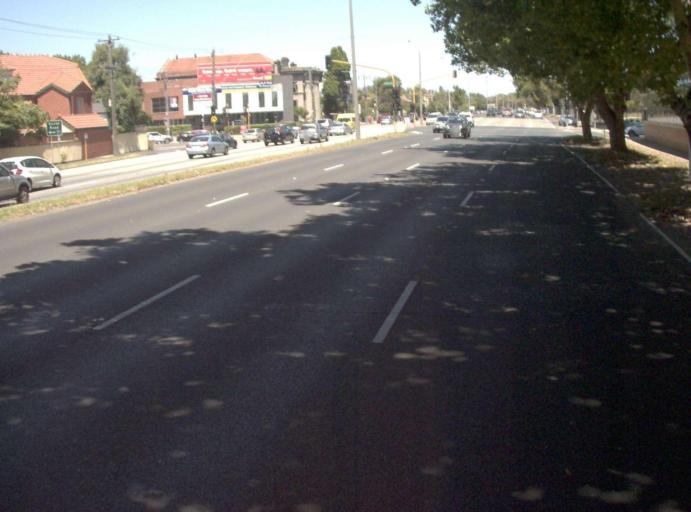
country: AU
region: Victoria
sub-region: Stonnington
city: Malvern East
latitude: -37.8773
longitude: 145.0467
